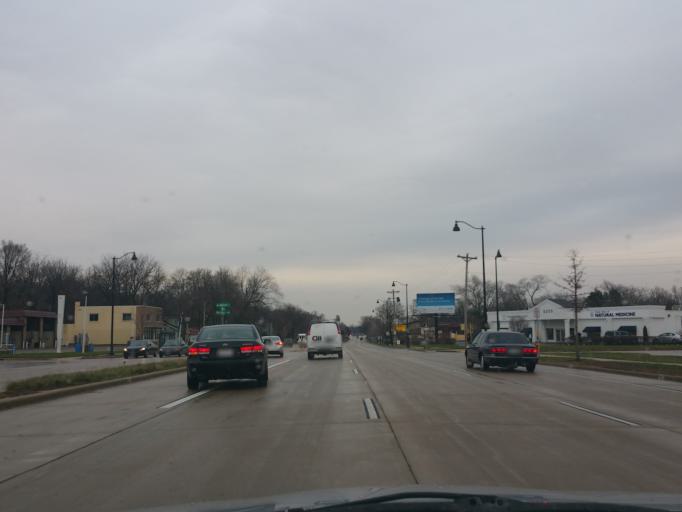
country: US
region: Wisconsin
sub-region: Dane County
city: Maple Bluff
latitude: 43.1088
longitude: -89.3365
